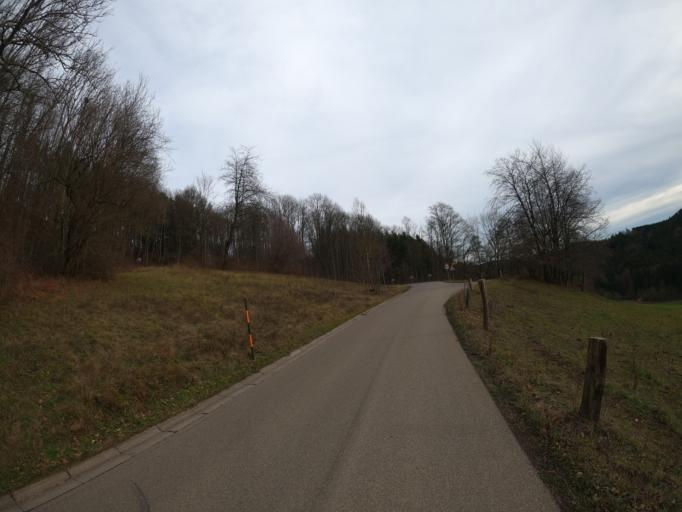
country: DE
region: Baden-Wuerttemberg
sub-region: Regierungsbezirk Stuttgart
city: Ottenbach
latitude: 48.7531
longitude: 9.7764
